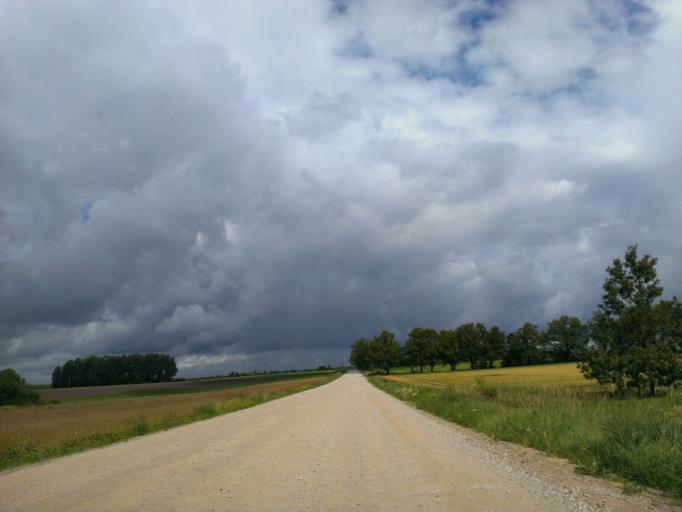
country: LV
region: Sigulda
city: Sigulda
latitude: 57.1735
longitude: 24.9212
